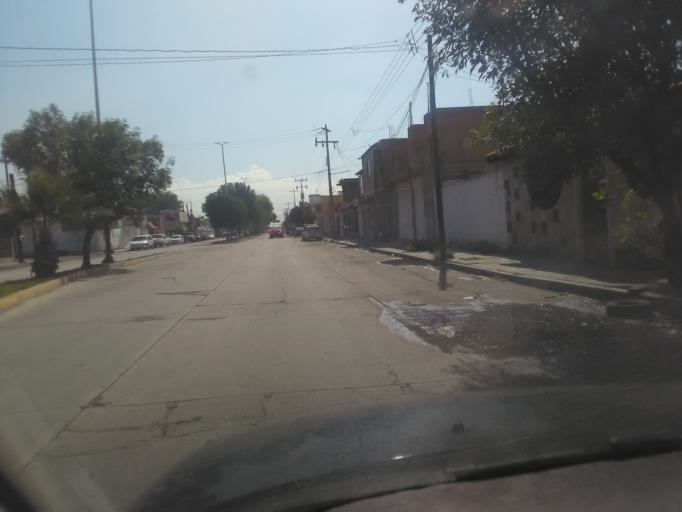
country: MX
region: Durango
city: Victoria de Durango
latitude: 24.0205
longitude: -104.6278
